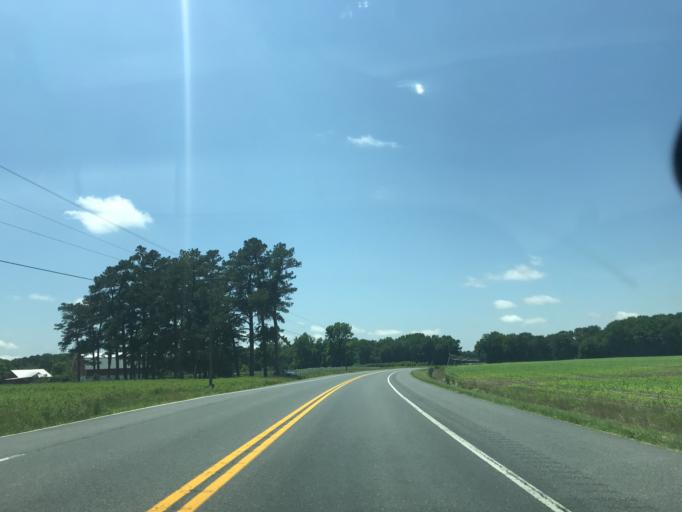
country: US
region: Maryland
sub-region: Caroline County
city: Federalsburg
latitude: 38.6311
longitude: -75.7195
